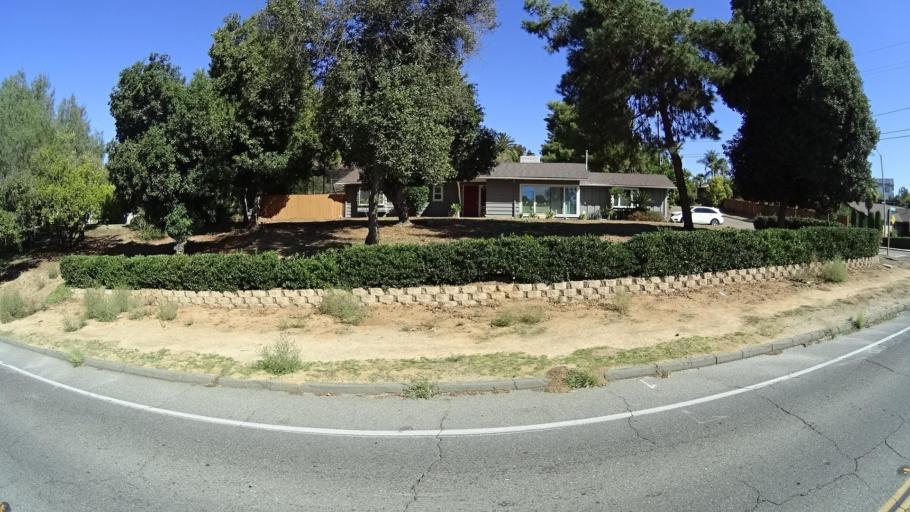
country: US
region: California
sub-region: San Diego County
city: Winter Gardens
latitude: 32.8201
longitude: -116.9202
